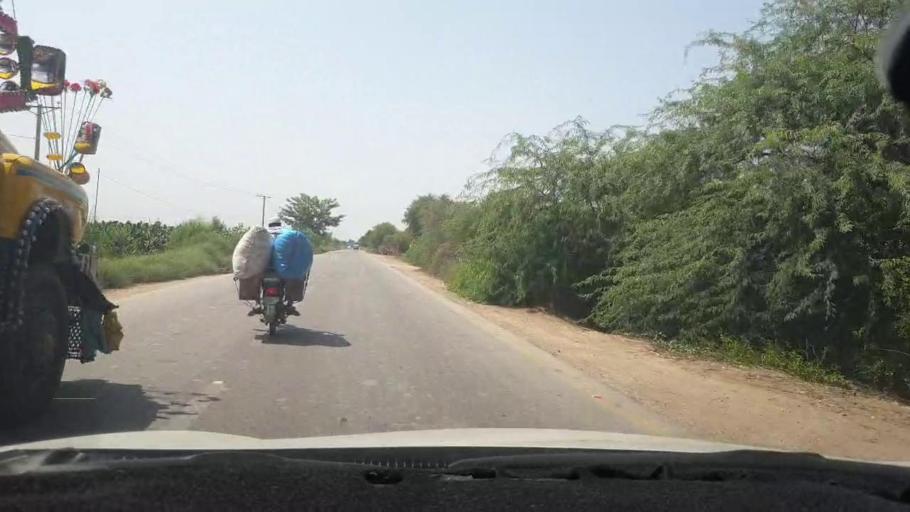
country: PK
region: Sindh
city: Bhit Shah
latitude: 25.8622
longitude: 68.5147
